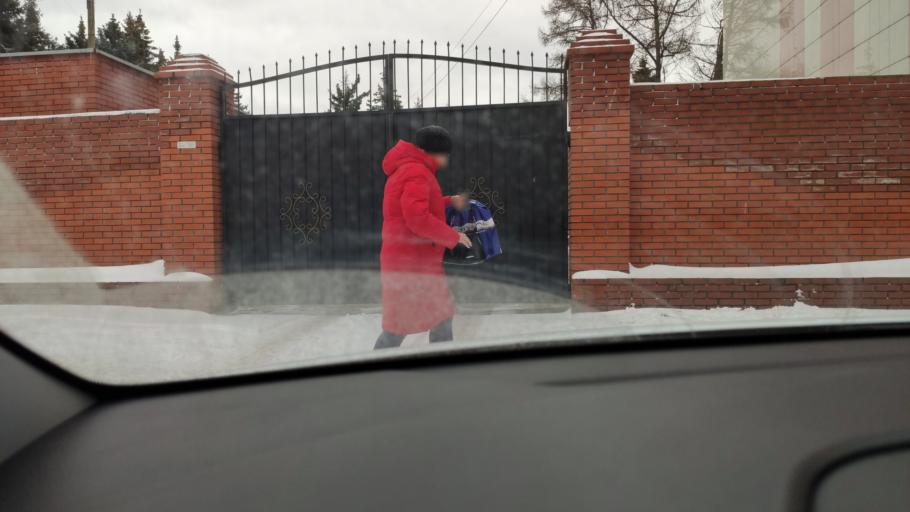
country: RU
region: Tatarstan
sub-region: Gorod Kazan'
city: Kazan
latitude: 55.7424
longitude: 49.1439
